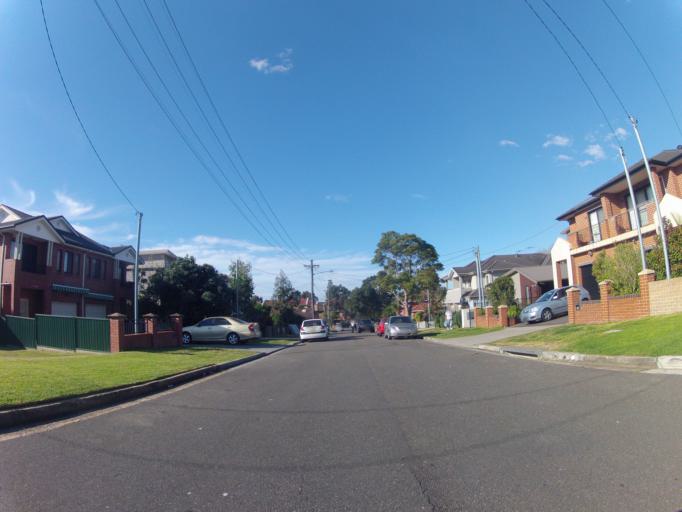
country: AU
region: New South Wales
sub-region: Hurstville
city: Penshurst
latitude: -33.9536
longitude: 151.0797
